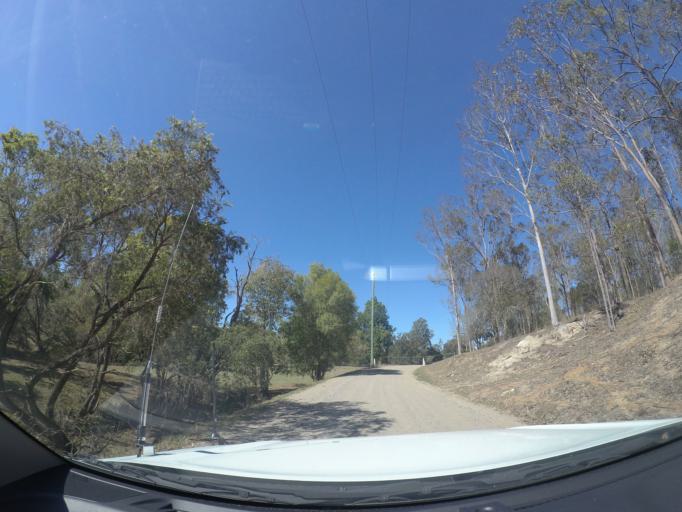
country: AU
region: Queensland
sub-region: Ipswich
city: Springfield Lakes
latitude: -27.7489
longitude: 152.9067
